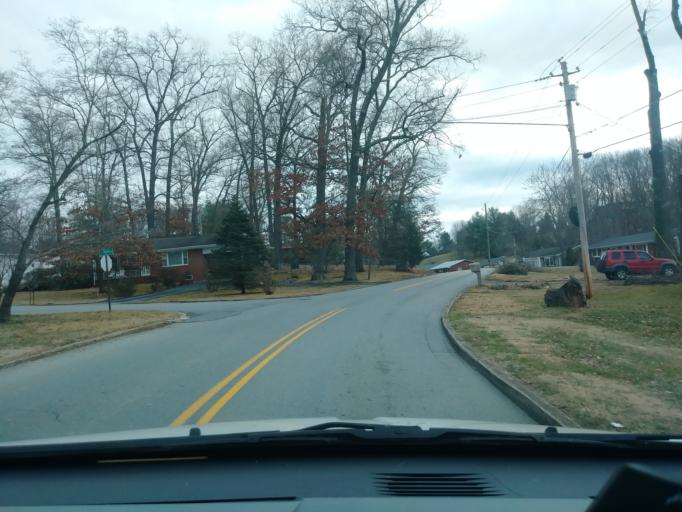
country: US
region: Tennessee
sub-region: Greene County
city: Tusculum
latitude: 36.1748
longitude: -82.7829
